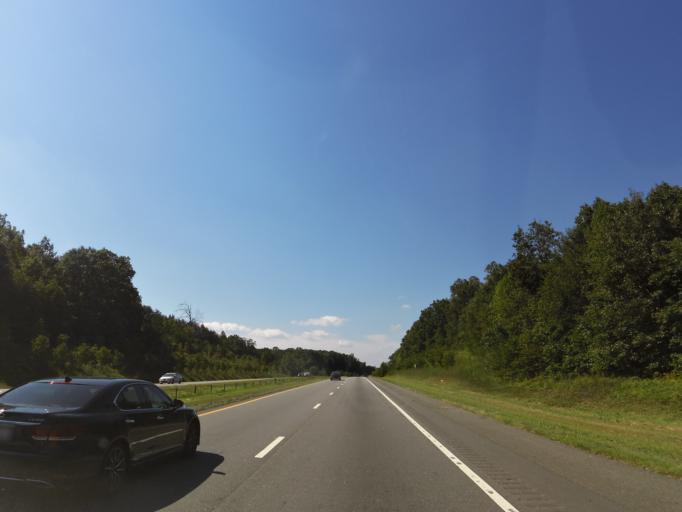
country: US
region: North Carolina
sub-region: Catawba County
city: Mountain View
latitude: 35.6472
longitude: -81.3078
